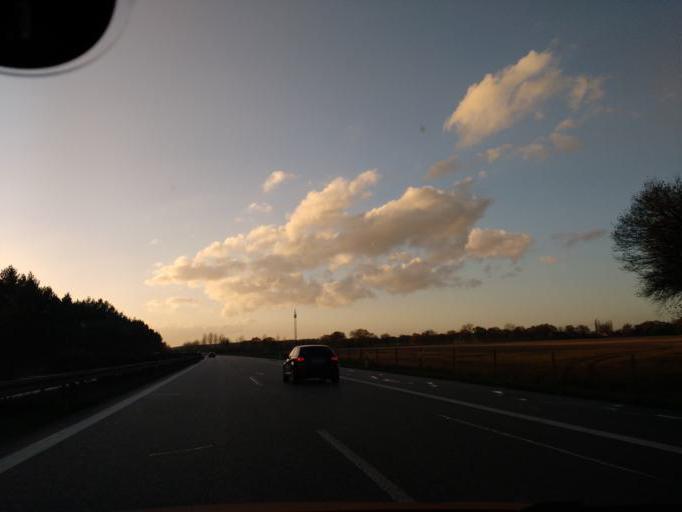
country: DE
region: Mecklenburg-Vorpommern
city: Hagenow
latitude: 53.4882
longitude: 11.2465
